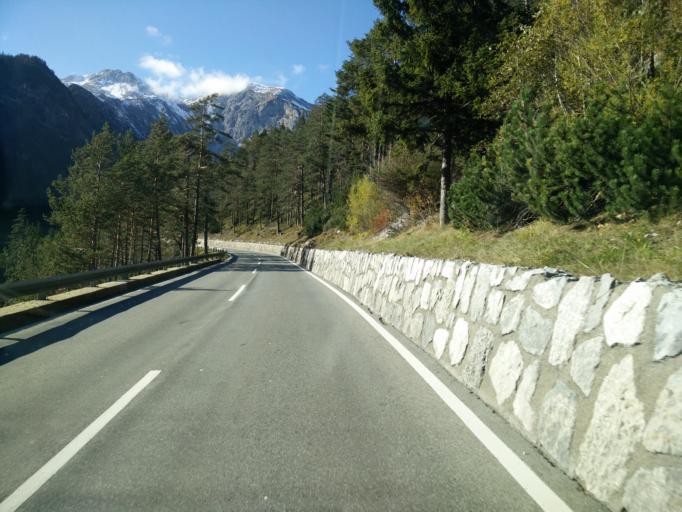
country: AT
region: Tyrol
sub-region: Politischer Bezirk Imst
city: Nassereith
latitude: 47.3560
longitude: 10.8286
